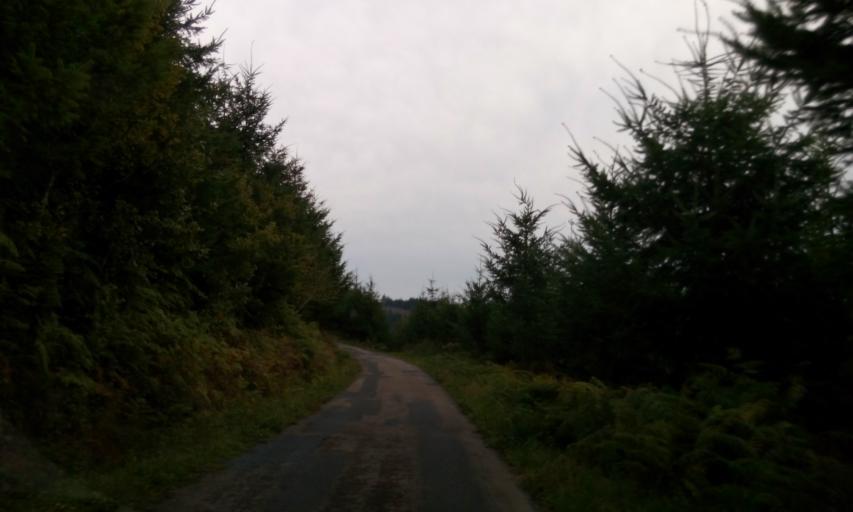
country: FR
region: Rhone-Alpes
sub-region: Departement du Rhone
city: Cublize
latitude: 46.0021
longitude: 4.4142
